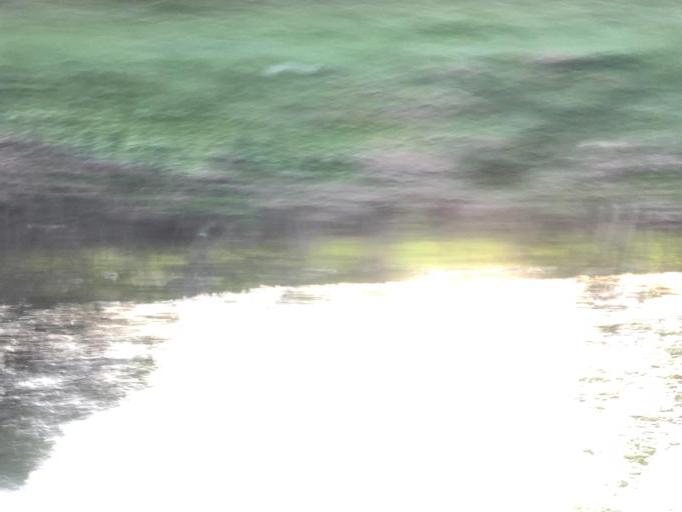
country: DE
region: Baden-Wuerttemberg
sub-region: Tuebingen Region
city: Pliezhausen
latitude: 48.5928
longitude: 9.1706
